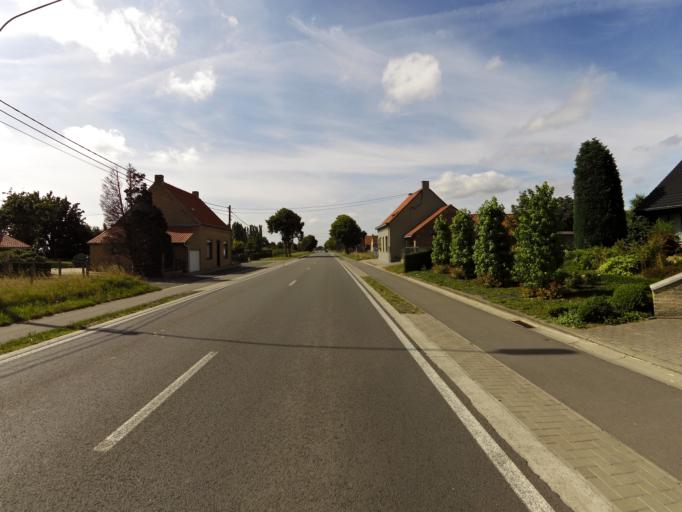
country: BE
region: Flanders
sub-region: Provincie West-Vlaanderen
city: Diksmuide
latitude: 50.9619
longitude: 2.8673
